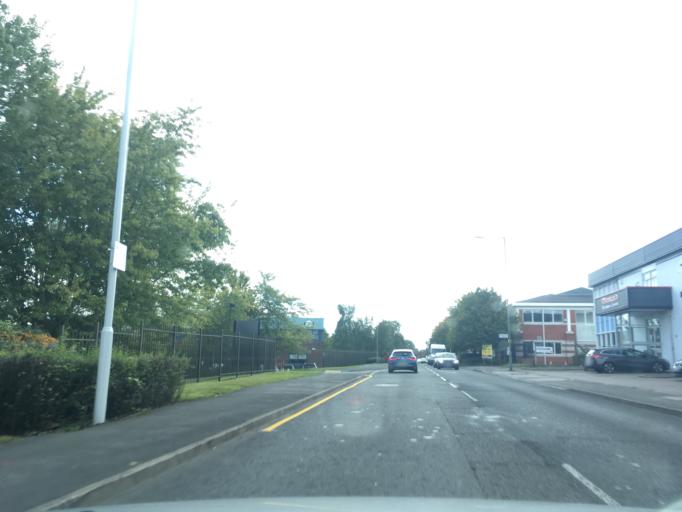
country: GB
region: England
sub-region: Buckinghamshire
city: High Wycombe
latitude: 51.6202
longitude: -0.7716
